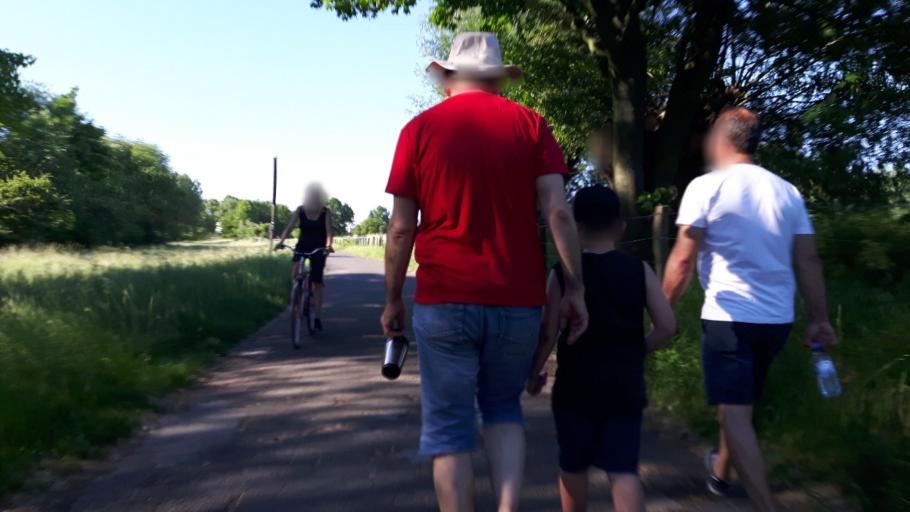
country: DE
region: North Rhine-Westphalia
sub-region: Regierungsbezirk Dusseldorf
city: Meerbusch
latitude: 51.3114
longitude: 6.7376
